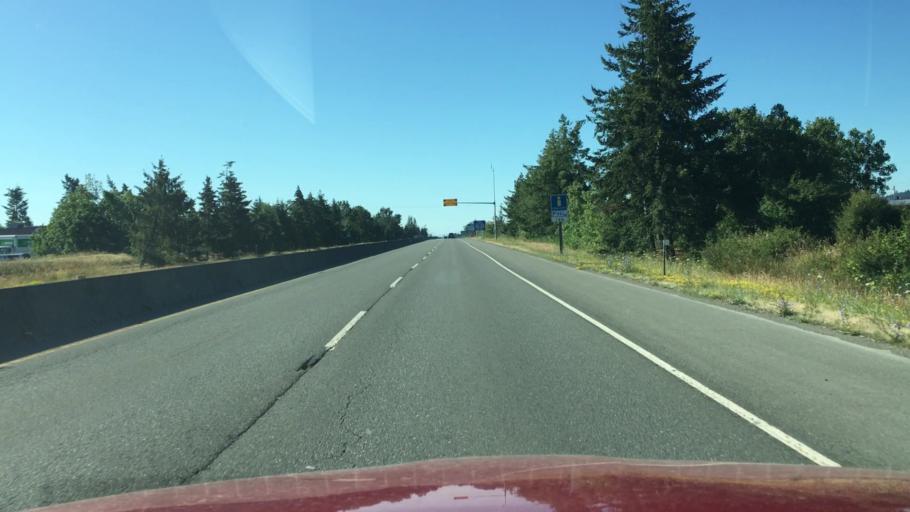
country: CA
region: British Columbia
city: North Saanich
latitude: 48.6585
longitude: -123.4141
